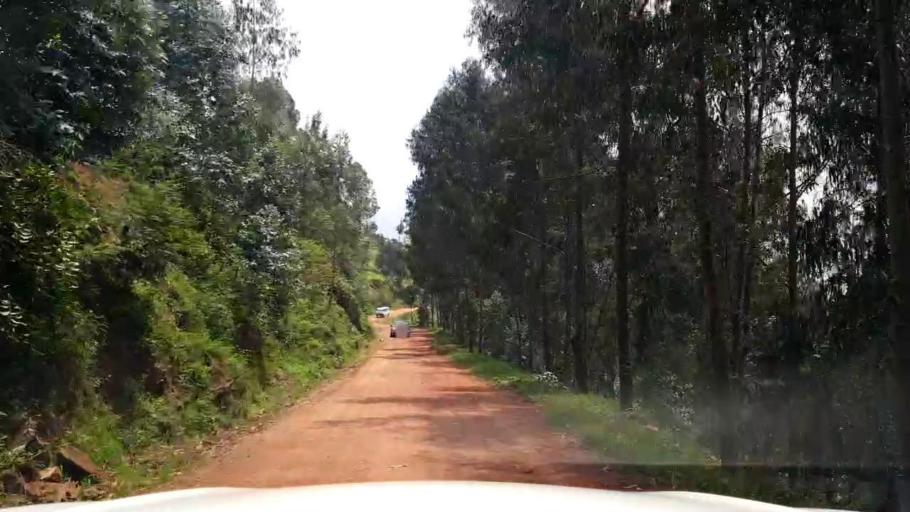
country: RW
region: Northern Province
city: Byumba
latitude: -1.4834
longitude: 29.9232
